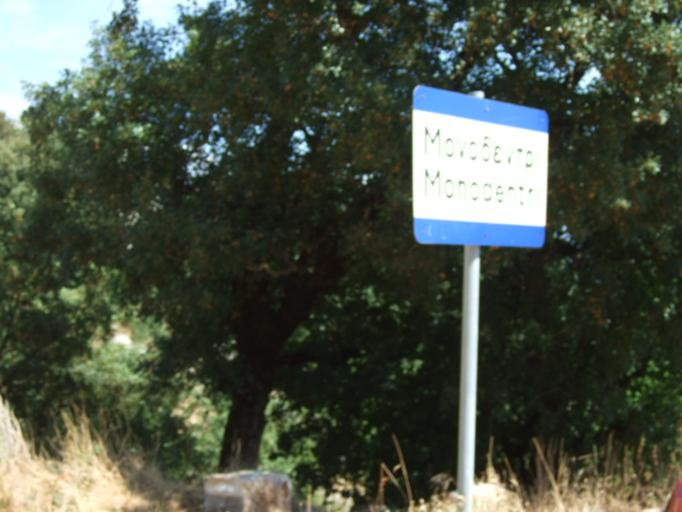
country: GR
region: Epirus
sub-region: Nomos Ioanninon
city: Asprangeloi
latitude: 39.8827
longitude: 20.7439
